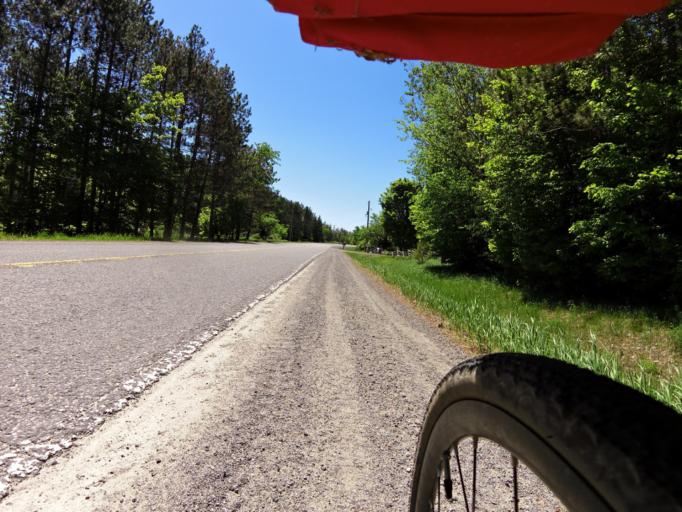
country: CA
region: Ontario
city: Carleton Place
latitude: 45.1845
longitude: -76.3602
